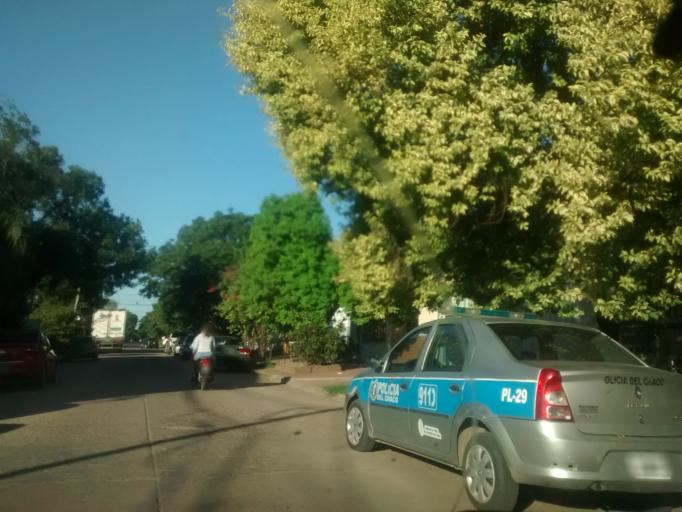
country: AR
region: Chaco
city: Resistencia
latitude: -27.4397
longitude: -58.9988
